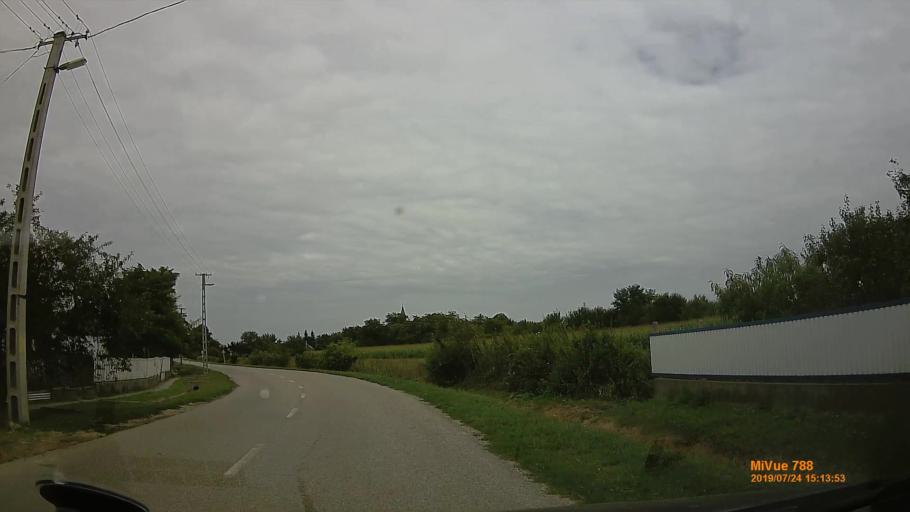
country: HU
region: Szabolcs-Szatmar-Bereg
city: Tarpa
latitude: 48.1999
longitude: 22.5194
